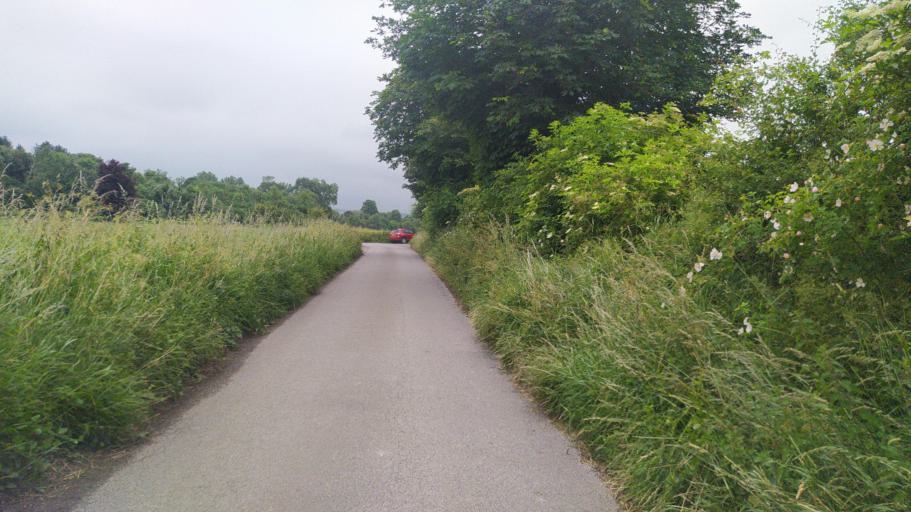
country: GB
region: England
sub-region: Wiltshire
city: Boyton
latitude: 51.1931
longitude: -2.1014
